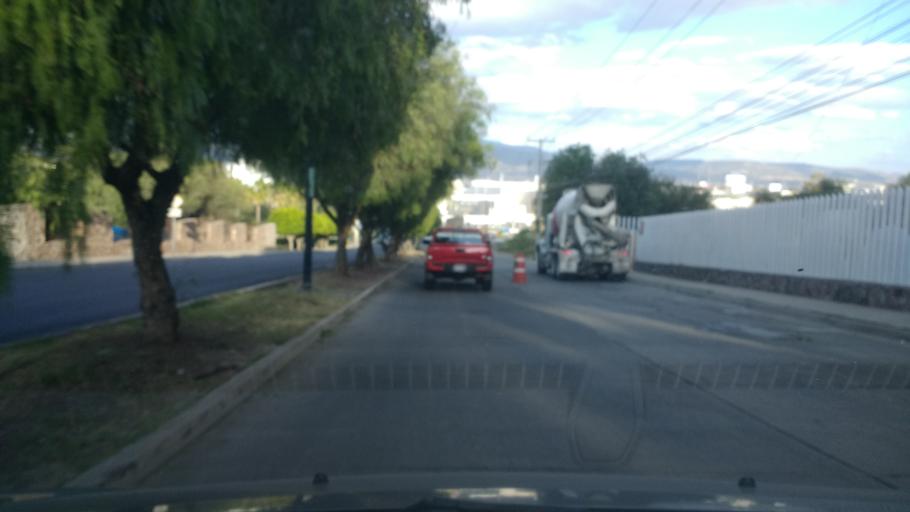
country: MX
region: Guanajuato
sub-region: Leon
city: La Ermita
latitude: 21.1579
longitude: -101.7008
